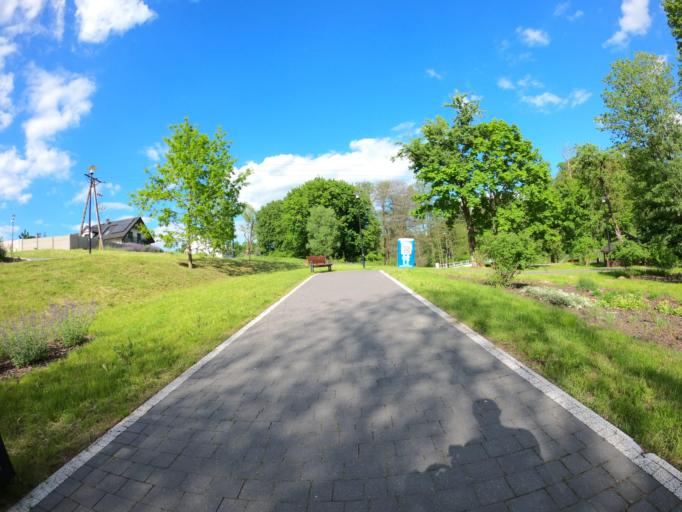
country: PL
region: Warmian-Masurian Voivodeship
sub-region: Powiat lidzbarski
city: Lidzbark Warminski
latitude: 54.1277
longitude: 20.5897
